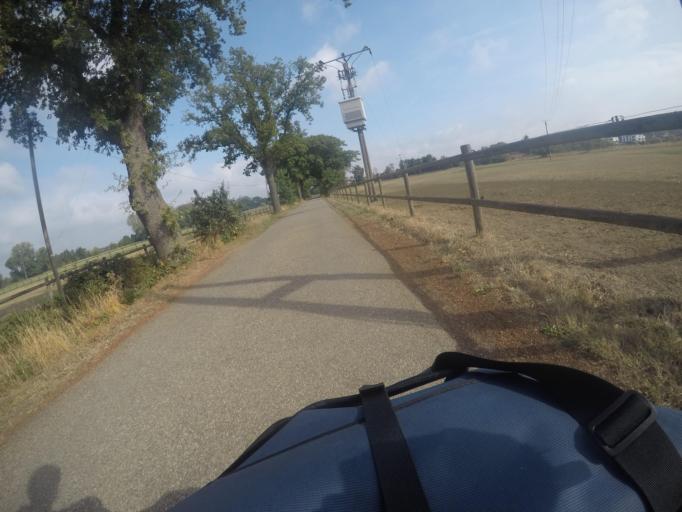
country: DE
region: North Rhine-Westphalia
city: Geldern
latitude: 51.5071
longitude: 6.3159
